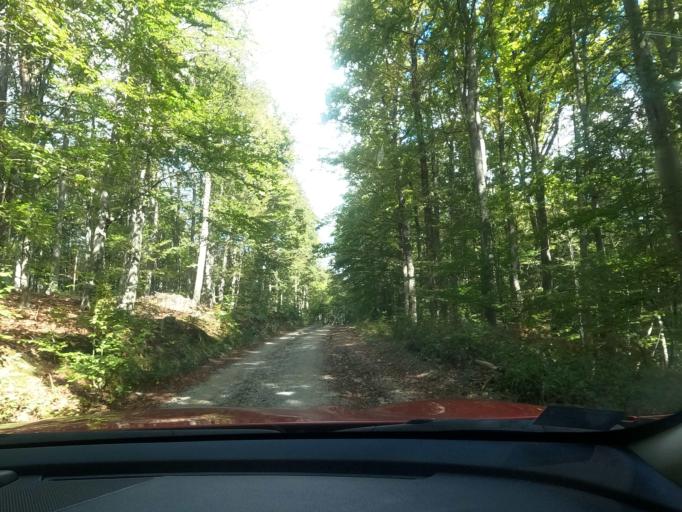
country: BA
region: Federation of Bosnia and Herzegovina
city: Velika Kladusa
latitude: 45.2515
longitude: 15.7692
